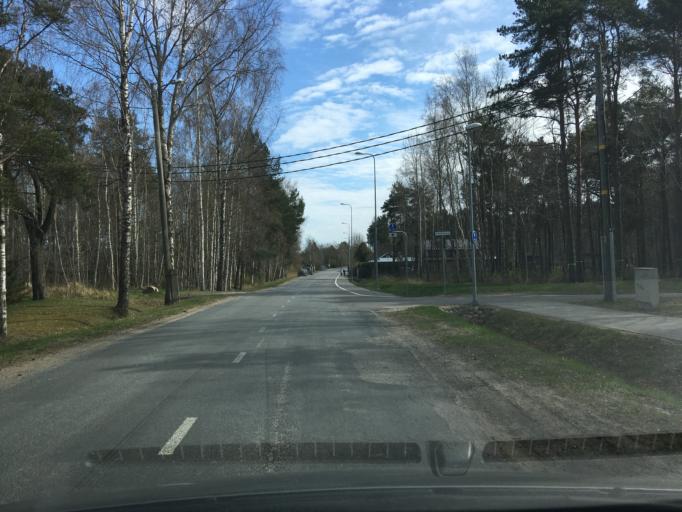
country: EE
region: Harju
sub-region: Joelaehtme vald
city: Loo
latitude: 59.4784
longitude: 24.9470
